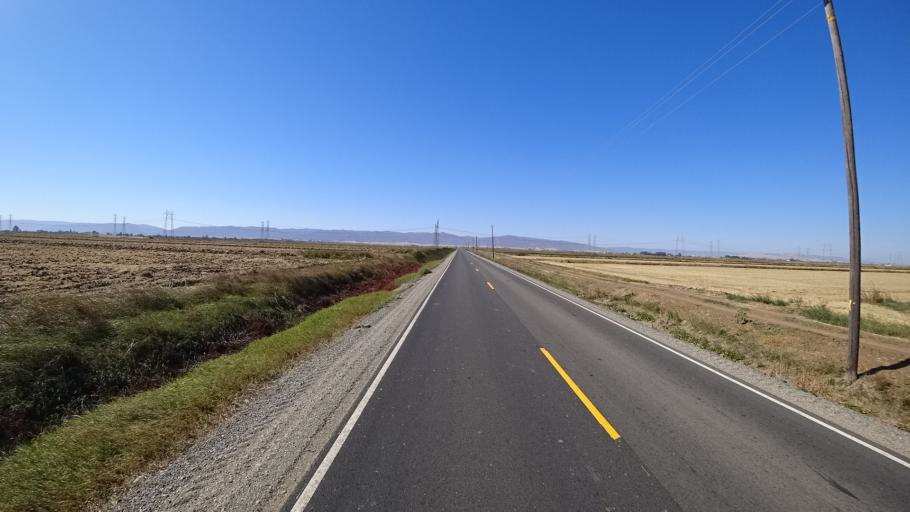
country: US
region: California
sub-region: Yolo County
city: Cottonwood
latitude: 38.6201
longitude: -121.9284
